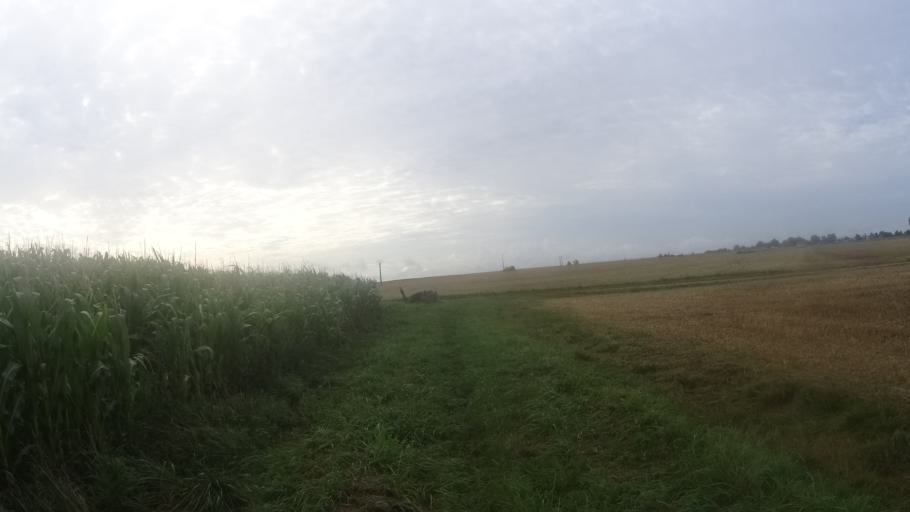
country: FR
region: Lorraine
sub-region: Departement de la Moselle
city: Niderviller
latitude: 48.7092
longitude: 7.0915
